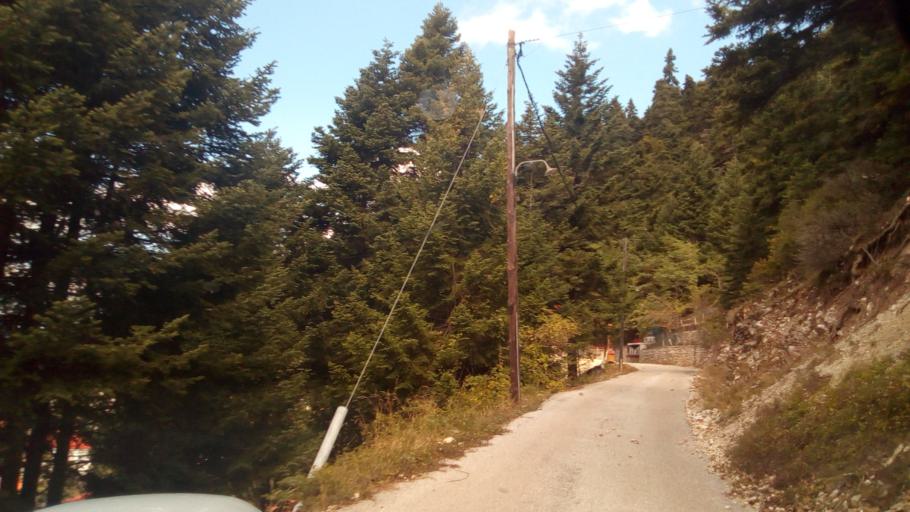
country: GR
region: West Greece
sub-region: Nomos Aitolias kai Akarnanias
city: Thermo
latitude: 38.6477
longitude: 21.9232
